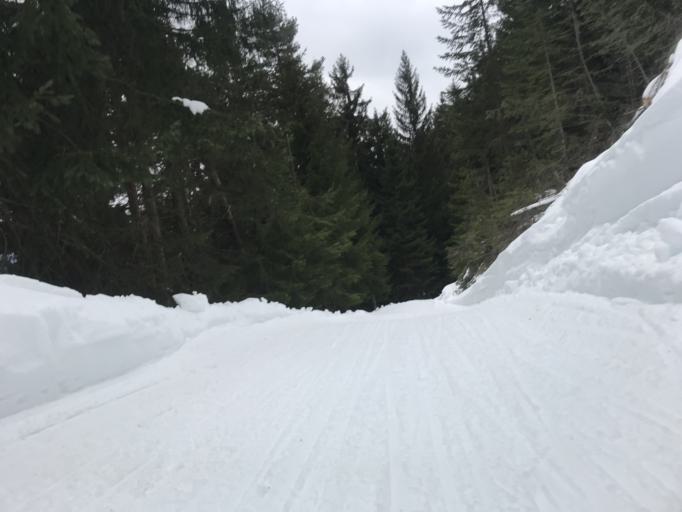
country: IT
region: Trentino-Alto Adige
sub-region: Bolzano
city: Funes - Villnoess
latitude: 46.6843
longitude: 11.6851
